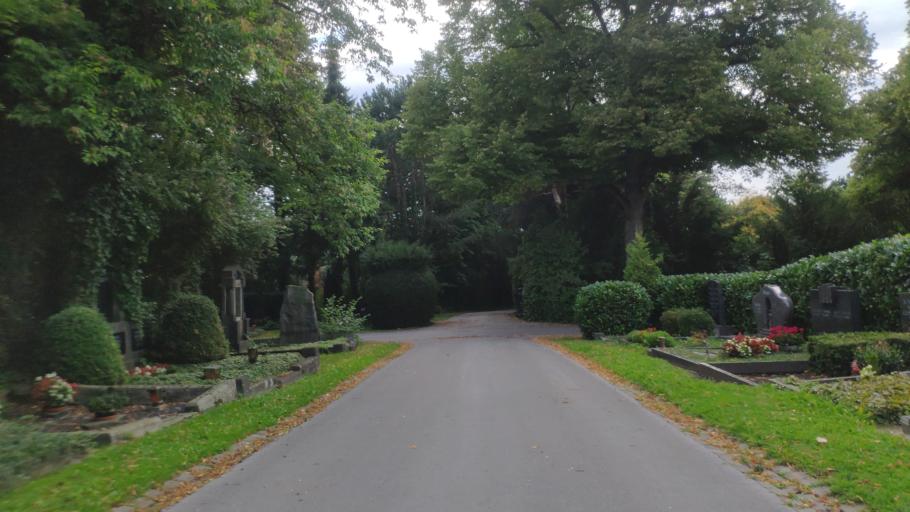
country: NL
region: Limburg
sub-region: Gemeente Vaals
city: Vaals
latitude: 50.7709
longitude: 6.0500
